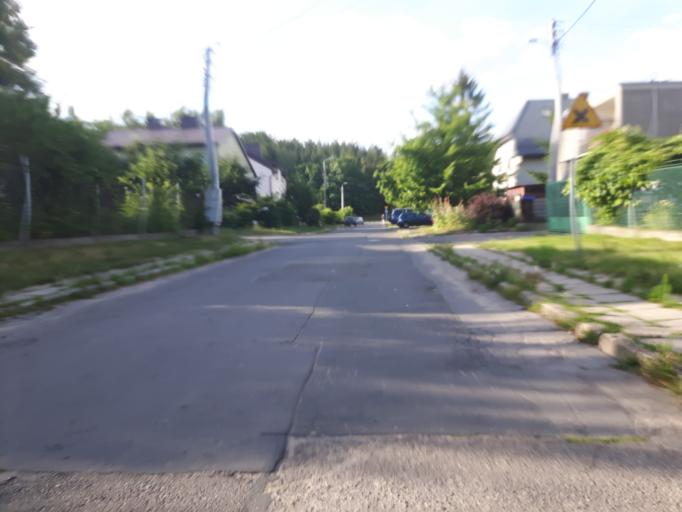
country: PL
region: Masovian Voivodeship
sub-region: Powiat wolominski
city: Zabki
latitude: 52.2957
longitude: 21.1170
